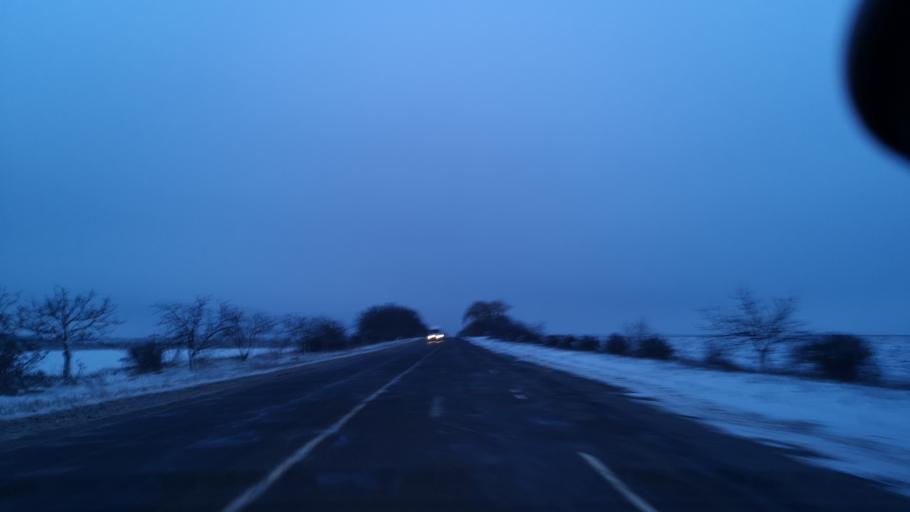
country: MD
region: Rezina
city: Rezina
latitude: 47.7469
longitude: 28.9250
